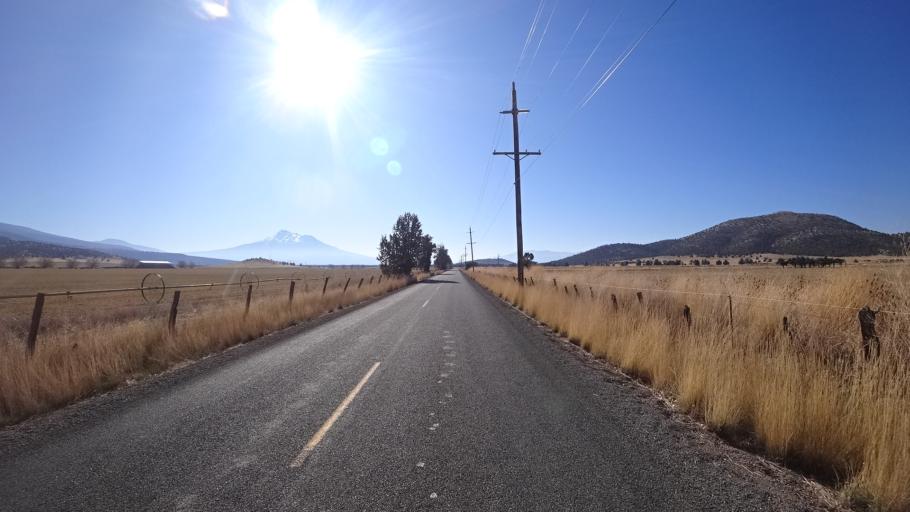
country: US
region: California
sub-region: Siskiyou County
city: Montague
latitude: 41.6836
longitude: -122.3697
